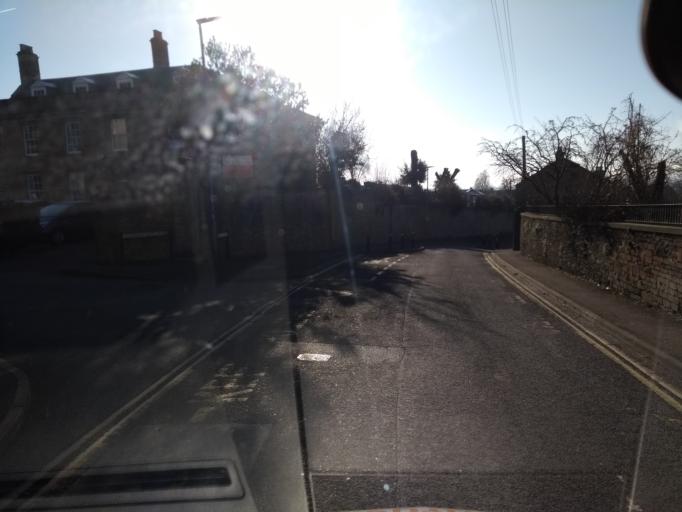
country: GB
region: England
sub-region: Somerset
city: Wincanton
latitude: 51.0550
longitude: -2.4102
